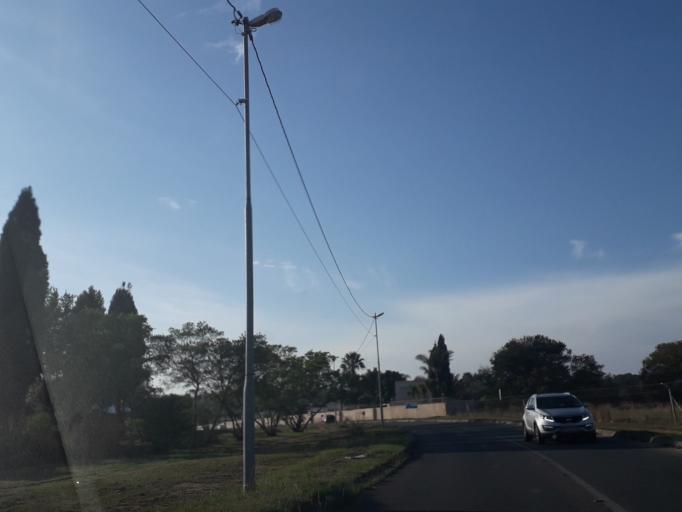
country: ZA
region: Gauteng
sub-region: City of Johannesburg Metropolitan Municipality
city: Roodepoort
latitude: -26.1003
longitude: 27.9178
